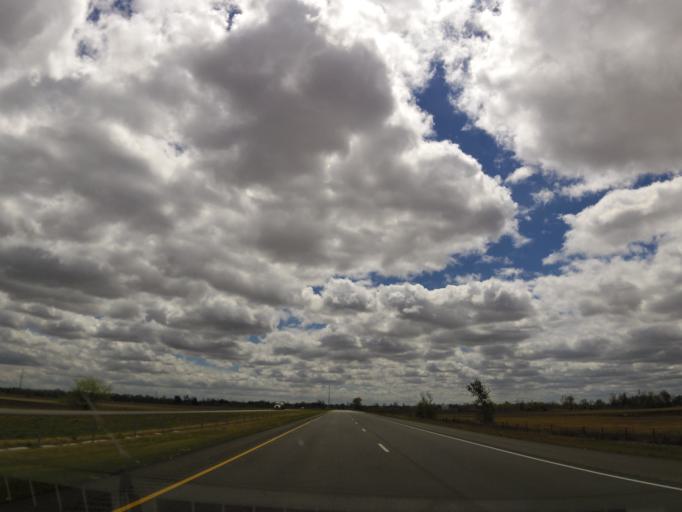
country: US
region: Arkansas
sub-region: Poinsett County
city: Marked Tree
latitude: 35.5595
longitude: -90.4969
